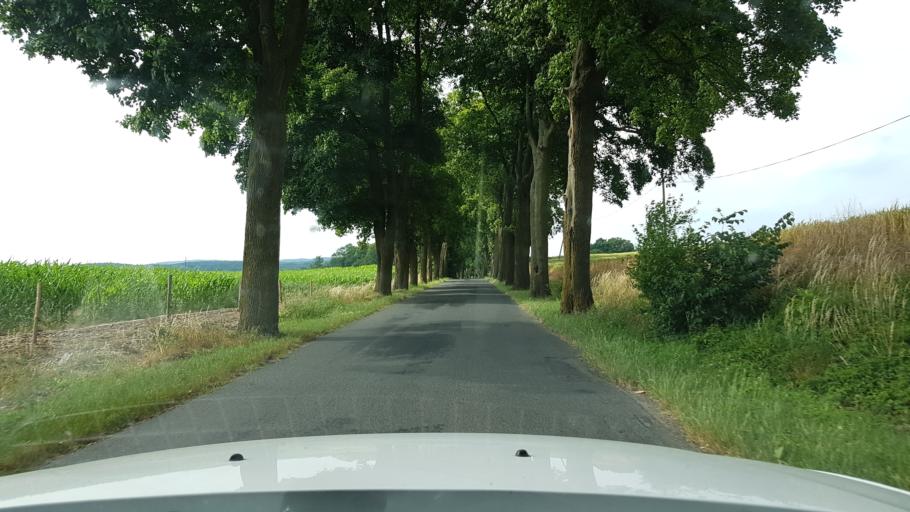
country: PL
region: West Pomeranian Voivodeship
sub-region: Powiat gryfinski
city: Moryn
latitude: 52.9124
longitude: 14.3678
